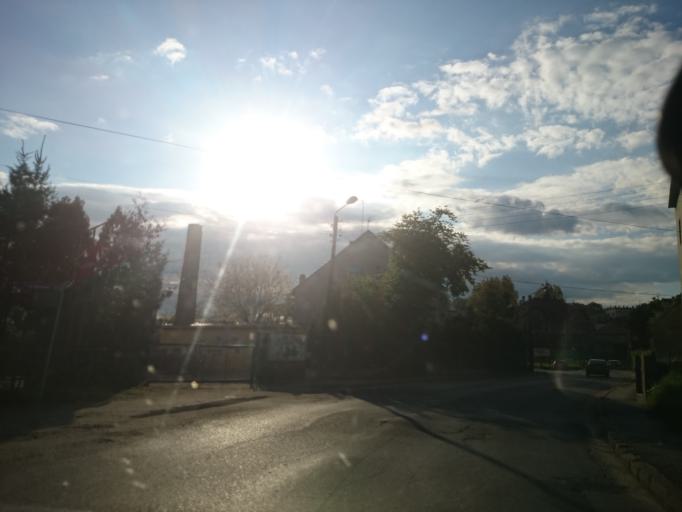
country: PL
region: Lower Silesian Voivodeship
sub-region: Powiat zabkowicki
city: Zabkowice Slaskie
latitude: 50.5849
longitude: 16.8128
